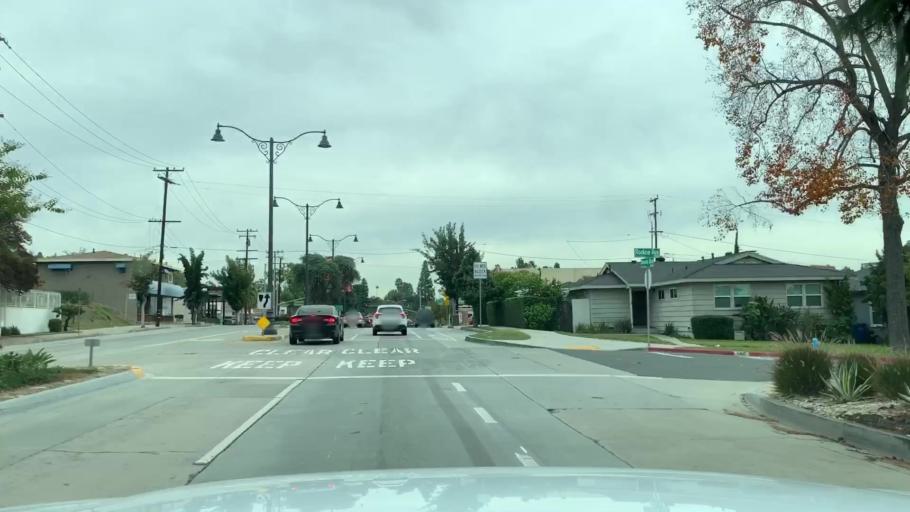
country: US
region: California
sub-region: Los Angeles County
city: West Whittier-Los Nietos
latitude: 33.9996
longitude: -118.0570
